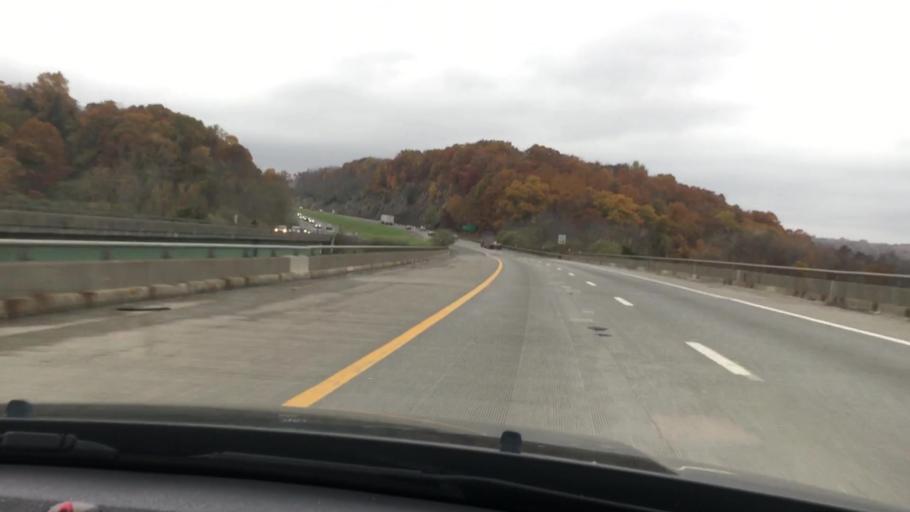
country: US
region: New York
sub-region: Putnam County
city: Brewster
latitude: 41.3991
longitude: -73.6010
